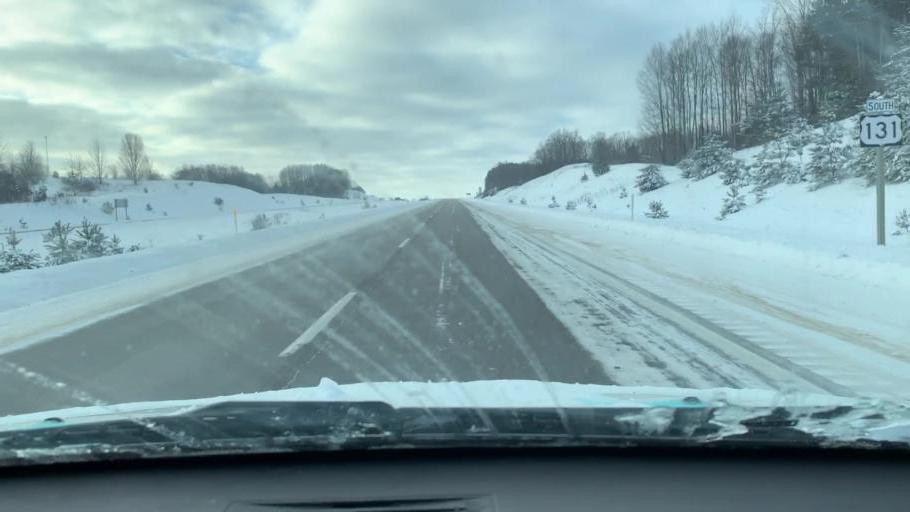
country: US
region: Michigan
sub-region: Wexford County
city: Manton
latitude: 44.3978
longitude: -85.3822
